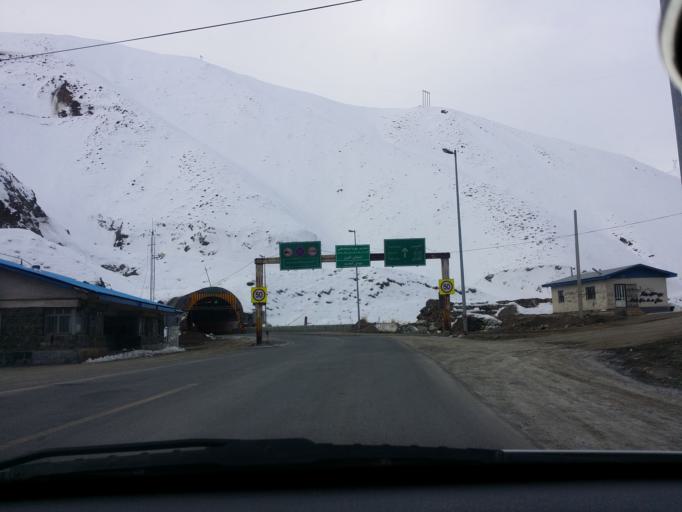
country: IR
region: Tehran
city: Tajrish
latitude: 36.1611
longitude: 51.3158
